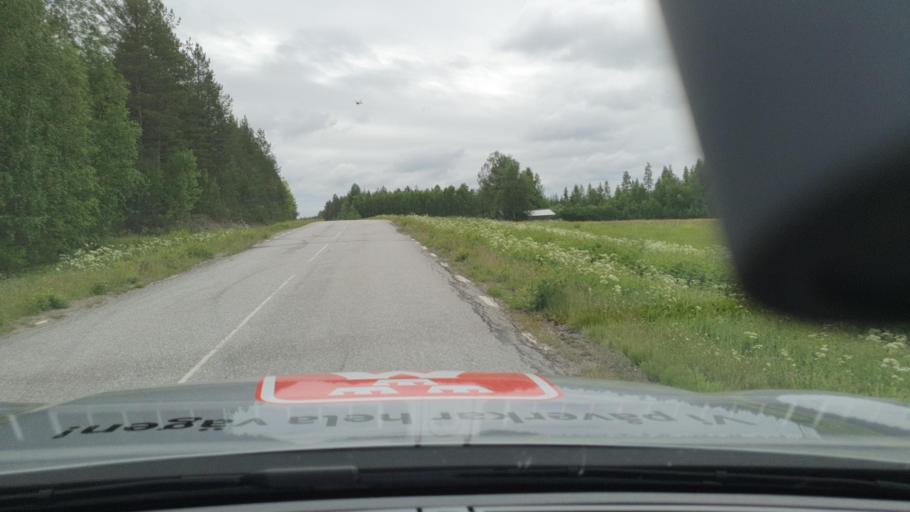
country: SE
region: Norrbotten
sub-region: Lulea Kommun
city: Ranea
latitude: 65.8918
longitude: 22.1885
